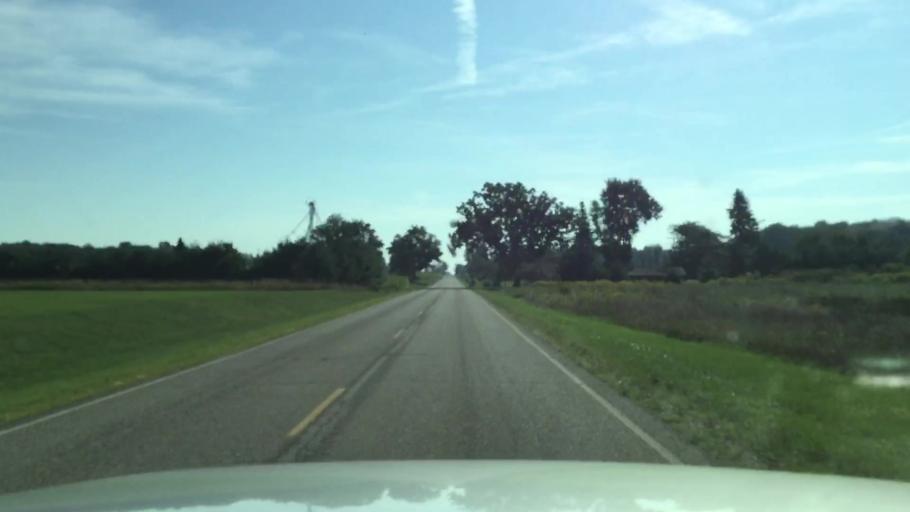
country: US
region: Michigan
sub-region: Lenawee County
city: Hudson
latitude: 41.9276
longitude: -84.4028
